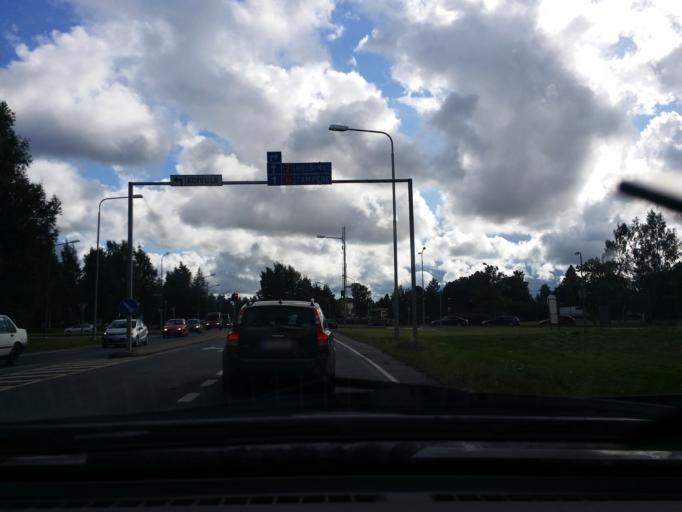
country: FI
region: Satakunta
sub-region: Pori
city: Pori
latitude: 61.4769
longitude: 21.8154
